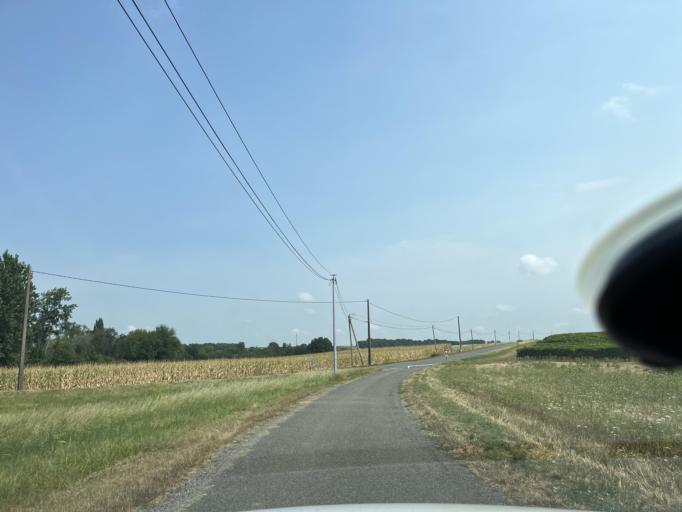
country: FR
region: Poitou-Charentes
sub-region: Departement de la Charente-Maritime
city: Pons
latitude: 45.5868
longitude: -0.5843
